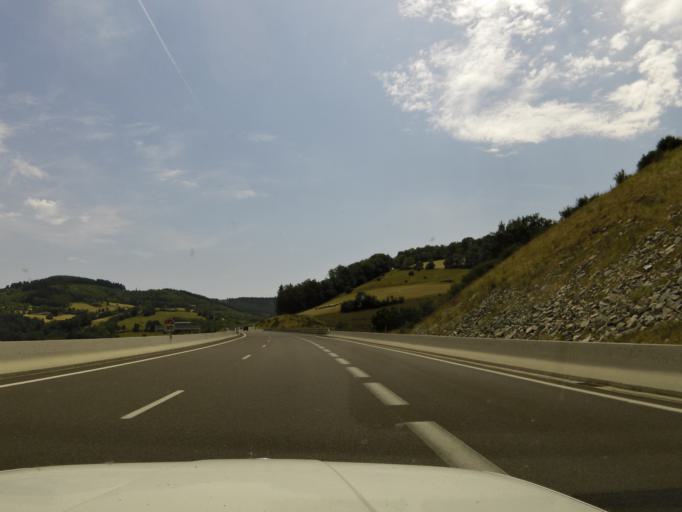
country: FR
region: Rhone-Alpes
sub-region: Departement du Rhone
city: Tarare
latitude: 45.8800
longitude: 4.3965
